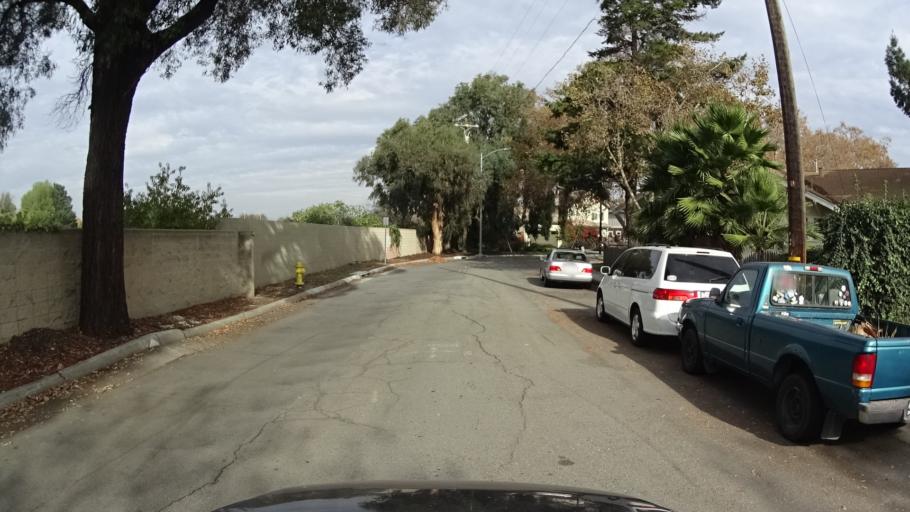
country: US
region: California
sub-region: Santa Clara County
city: Burbank
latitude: 37.3410
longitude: -121.9274
